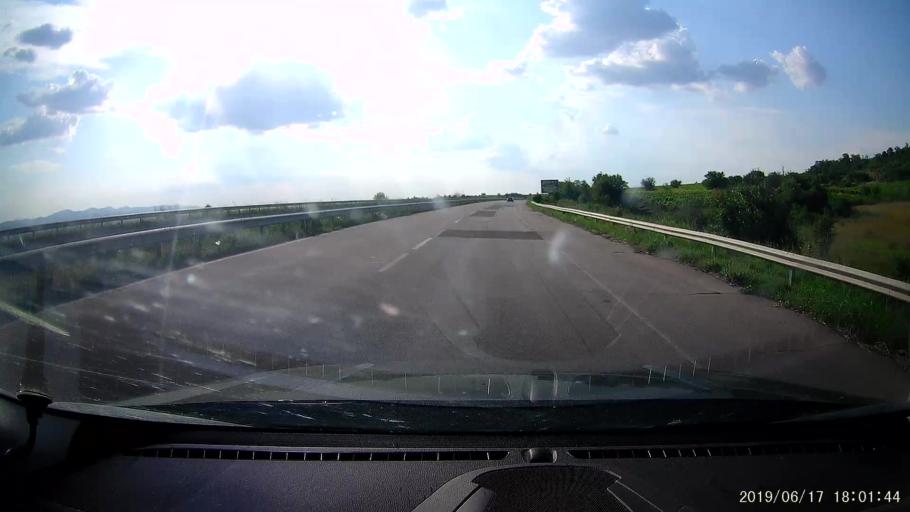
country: BG
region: Khaskovo
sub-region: Obshtina Svilengrad
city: Svilengrad
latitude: 41.7480
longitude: 26.2456
